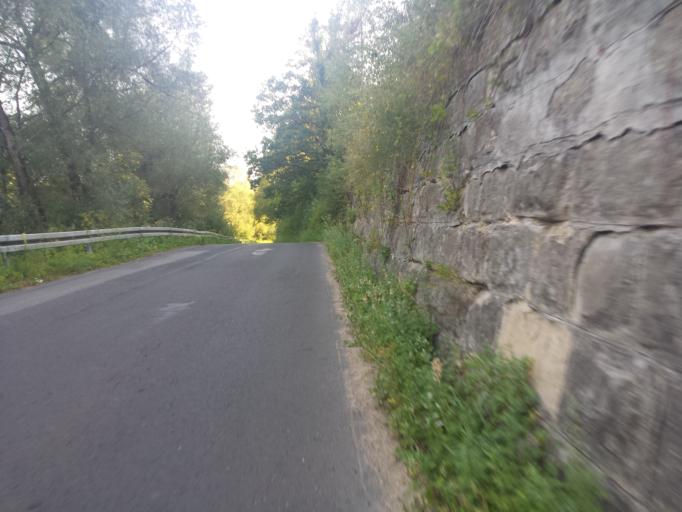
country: PL
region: Subcarpathian Voivodeship
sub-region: Powiat leski
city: Uherce Mineralne
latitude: 49.4602
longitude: 22.3963
